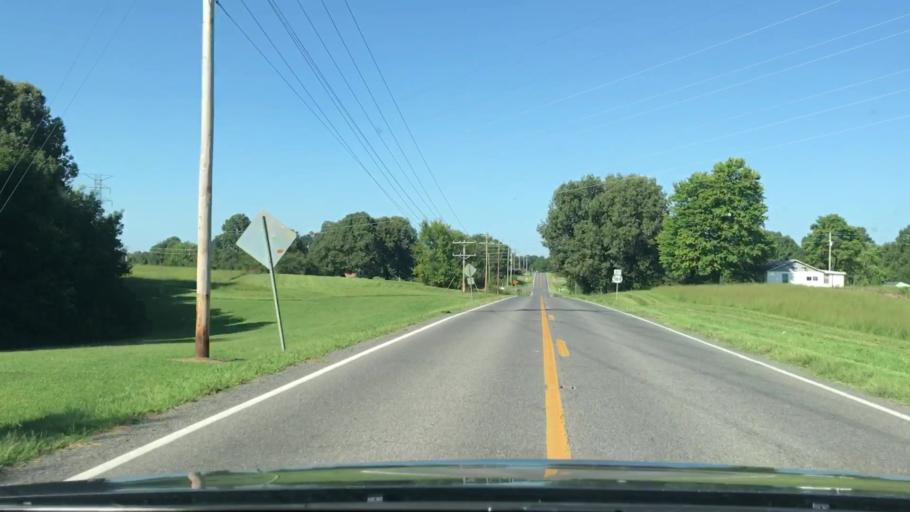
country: US
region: Kentucky
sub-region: Graves County
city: Mayfield
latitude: 36.7749
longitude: -88.4935
